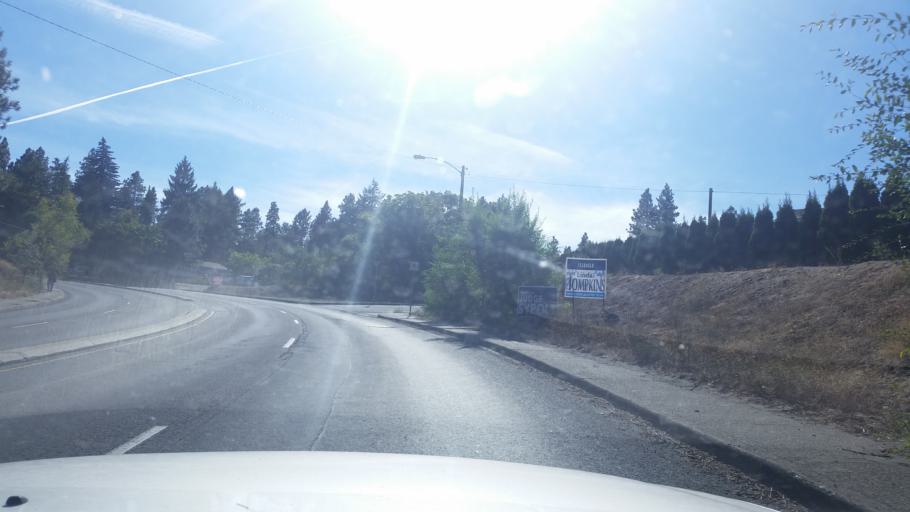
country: US
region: Washington
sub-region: Spokane County
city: Spokane
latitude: 47.6445
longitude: -117.3623
